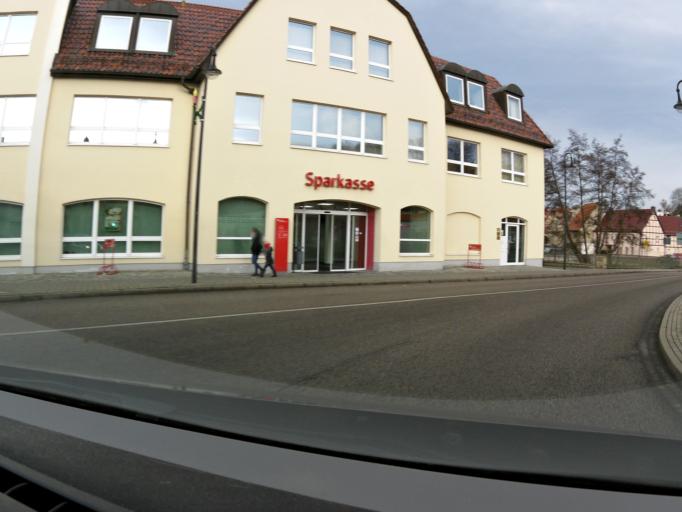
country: DE
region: Saxony-Anhalt
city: Hettstedt
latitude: 51.6443
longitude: 11.5123
